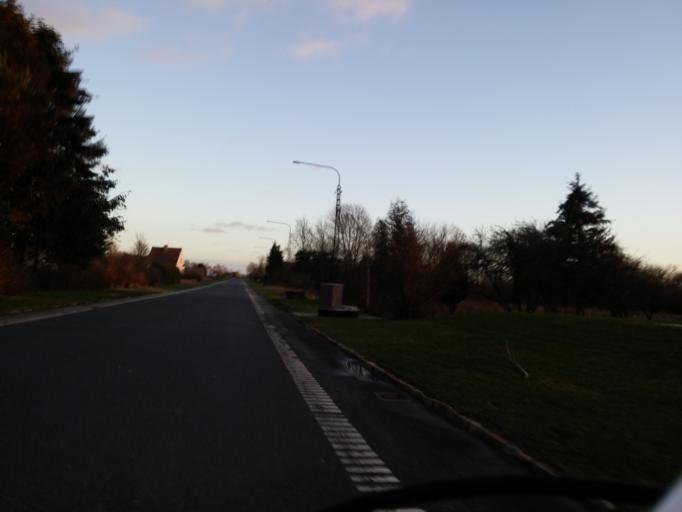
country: DK
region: South Denmark
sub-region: Kerteminde Kommune
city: Munkebo
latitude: 55.4648
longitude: 10.5428
